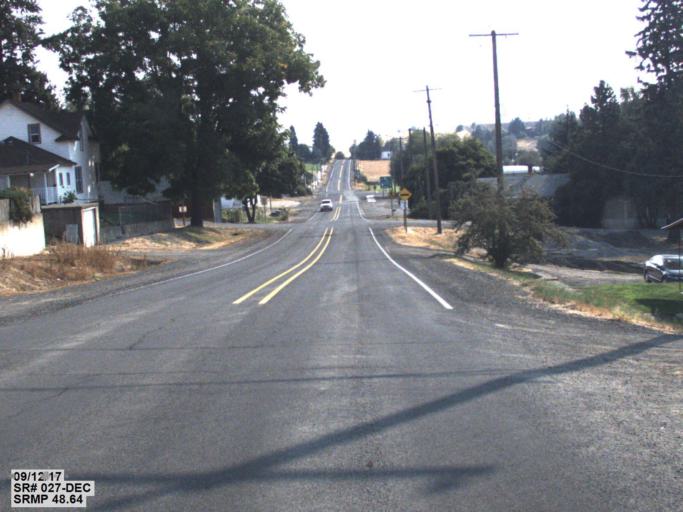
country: US
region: Idaho
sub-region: Benewah County
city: Plummer
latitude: 47.2268
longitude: -117.0760
